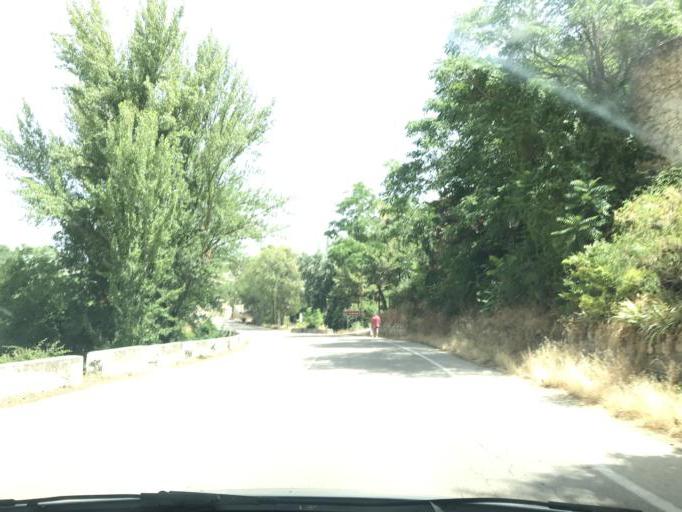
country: ES
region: Castille-La Mancha
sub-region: Provincia de Cuenca
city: Albalate de las Nogueras
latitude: 40.3680
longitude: -2.2778
